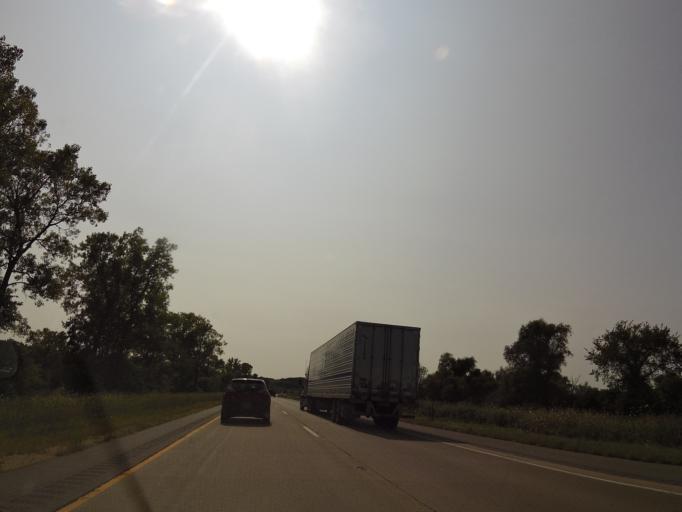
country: US
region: Wisconsin
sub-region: Monroe County
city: Tomah
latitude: 43.9506
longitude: -90.5434
